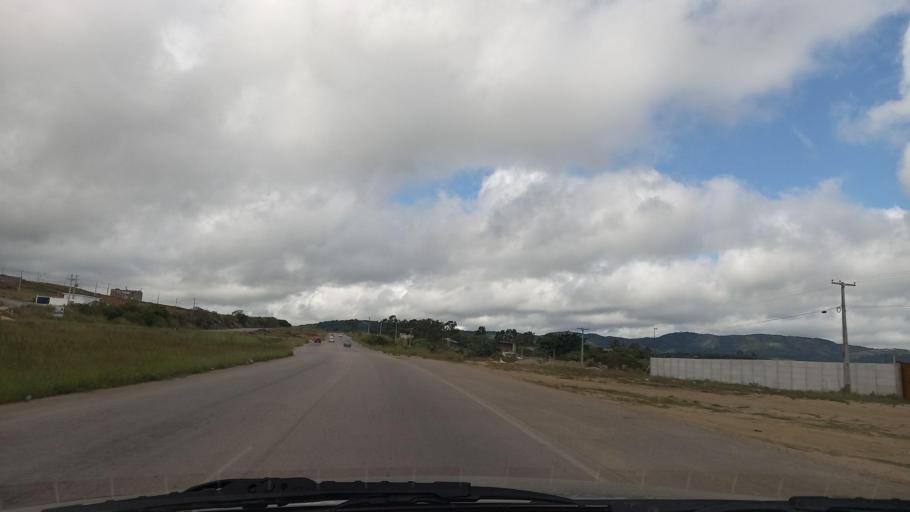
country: BR
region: Pernambuco
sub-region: Caruaru
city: Caruaru
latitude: -8.3150
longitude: -35.9914
